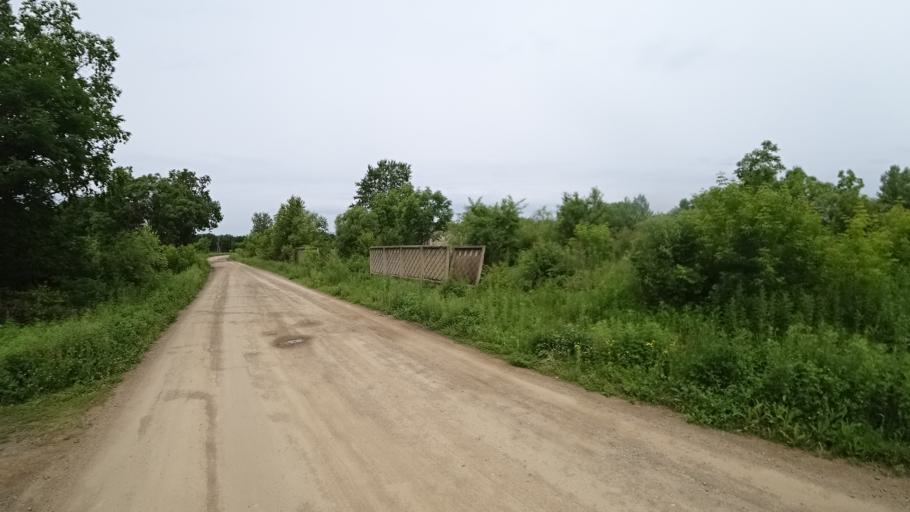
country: RU
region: Primorskiy
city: Arsen'yev
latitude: 44.1958
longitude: 133.3084
